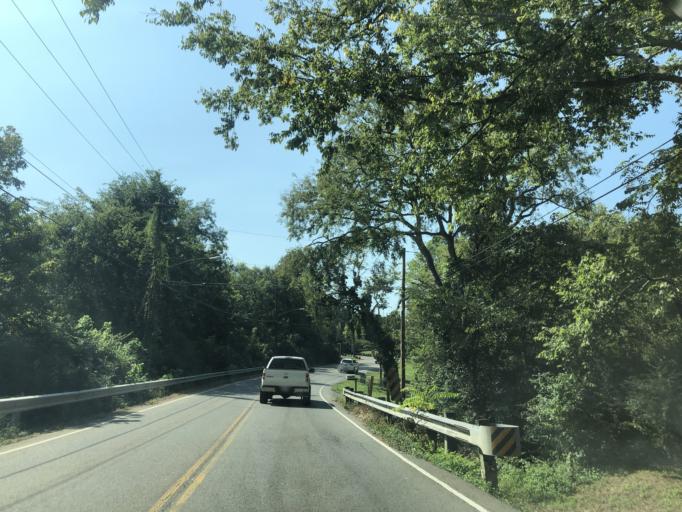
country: US
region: Tennessee
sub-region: Davidson County
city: Oak Hill
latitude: 36.0870
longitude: -86.7785
